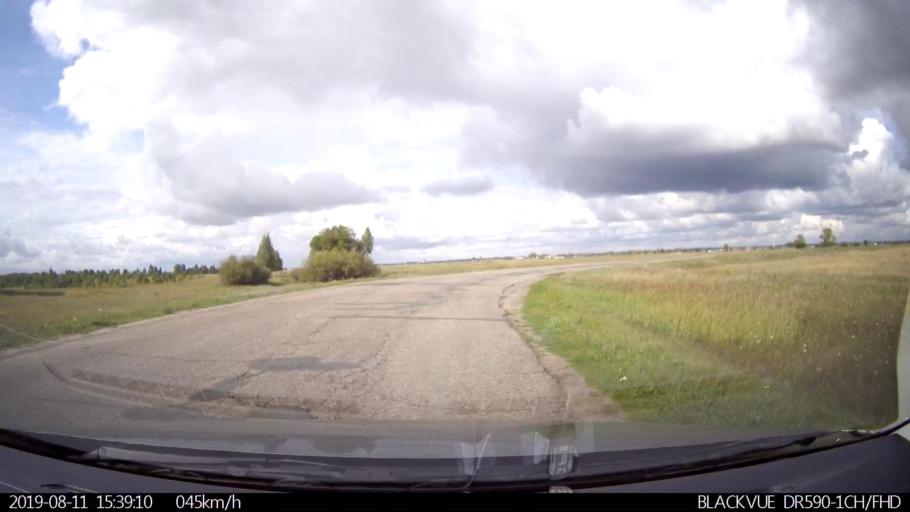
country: RU
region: Ulyanovsk
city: Ignatovka
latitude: 53.8664
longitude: 47.6393
